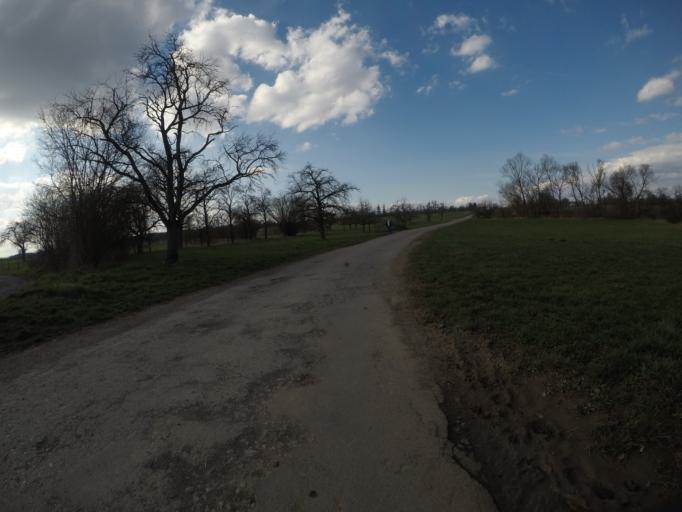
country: DE
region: Baden-Wuerttemberg
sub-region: Tuebingen Region
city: Ofterdingen
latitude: 48.4275
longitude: 9.0277
